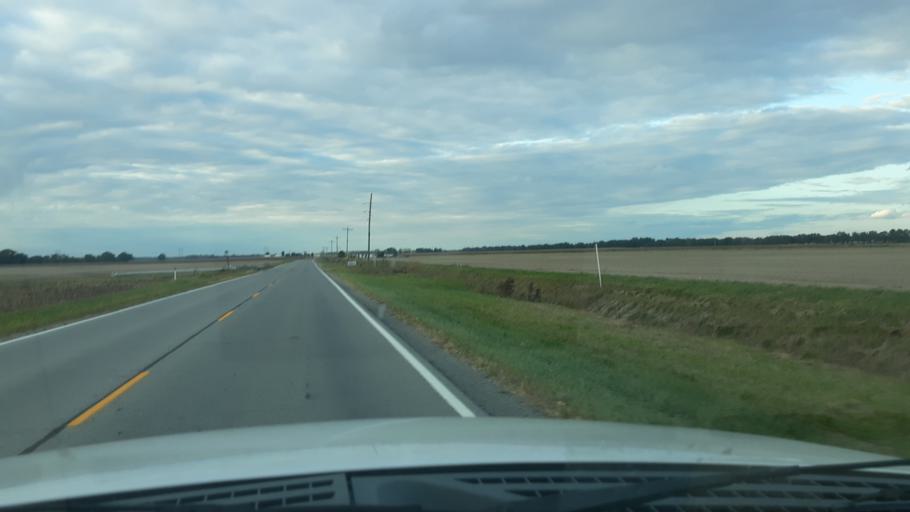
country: US
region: Illinois
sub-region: Saline County
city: Eldorado
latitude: 37.8366
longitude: -88.4525
